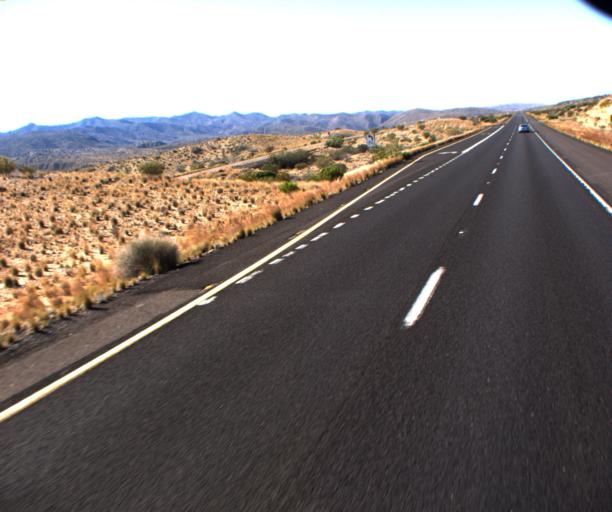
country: US
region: Arizona
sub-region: Mohave County
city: Kingman
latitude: 35.0589
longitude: -113.6656
